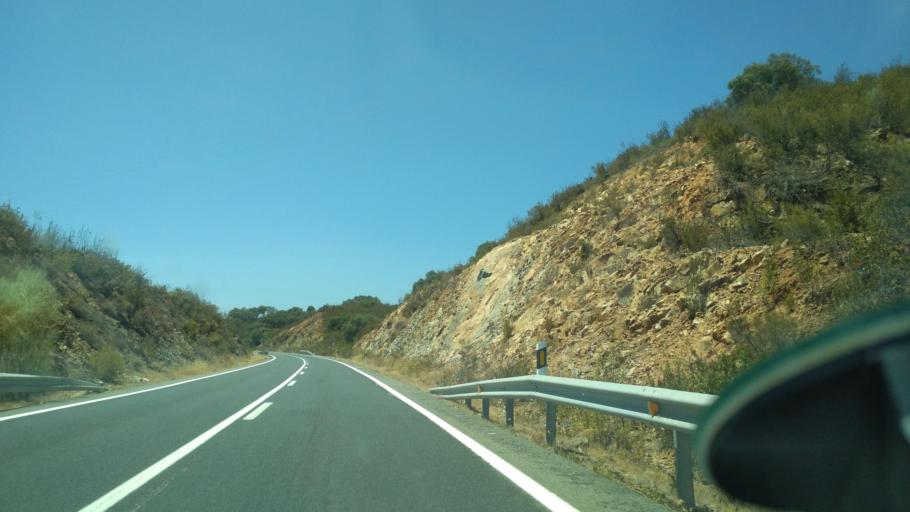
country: ES
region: Andalusia
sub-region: Provincia de Huelva
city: Aracena
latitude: 37.8547
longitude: -6.5666
